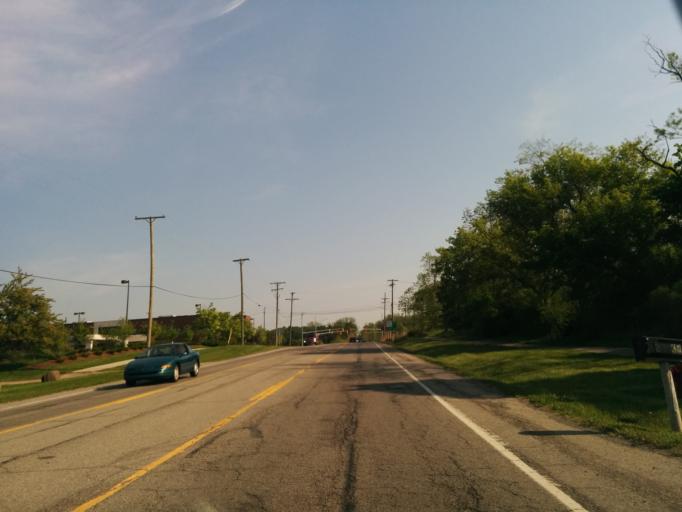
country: US
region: Michigan
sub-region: Oakland County
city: Novi
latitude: 42.4939
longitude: -83.4565
